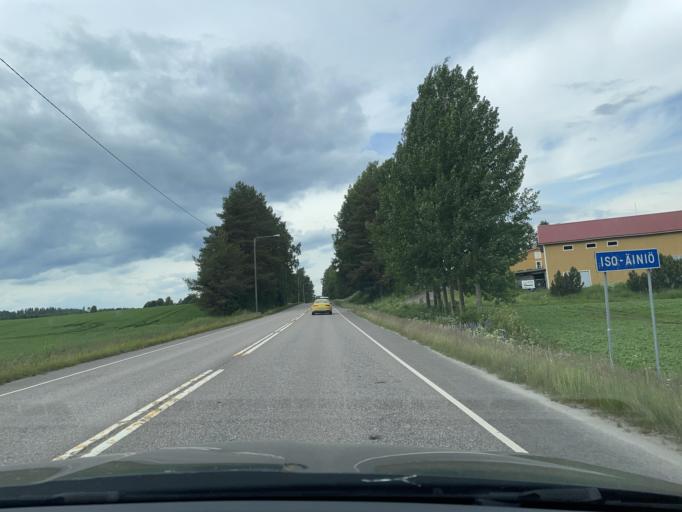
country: FI
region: Paijanne Tavastia
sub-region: Lahti
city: Asikkala
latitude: 61.2163
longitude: 25.3610
